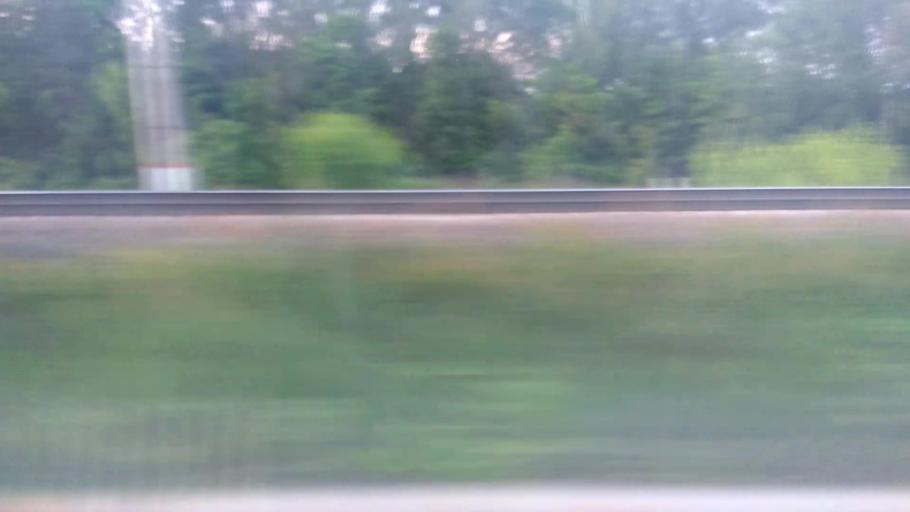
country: RU
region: Moskovskaya
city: Vostryakovo
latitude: 55.3749
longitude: 37.8203
